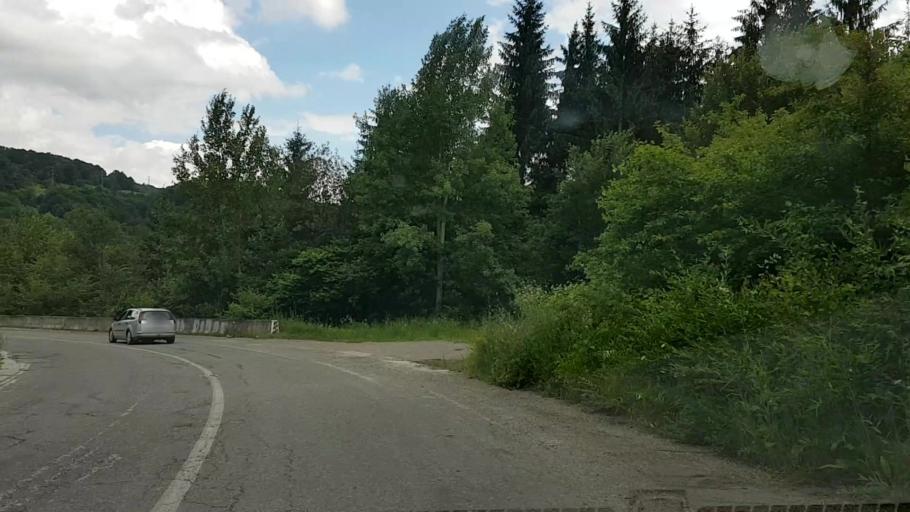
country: RO
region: Neamt
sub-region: Comuna Pangarati
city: Pangarati
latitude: 46.9507
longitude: 26.1259
